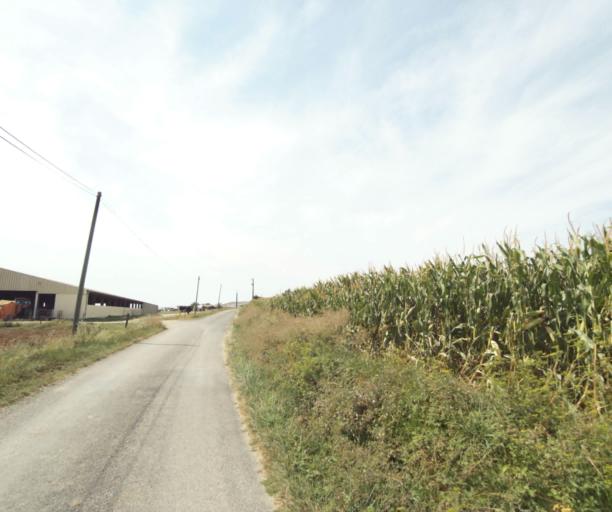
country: FR
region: Midi-Pyrenees
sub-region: Departement de la Haute-Garonne
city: Gaillac-Toulza
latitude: 43.2596
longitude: 1.4190
